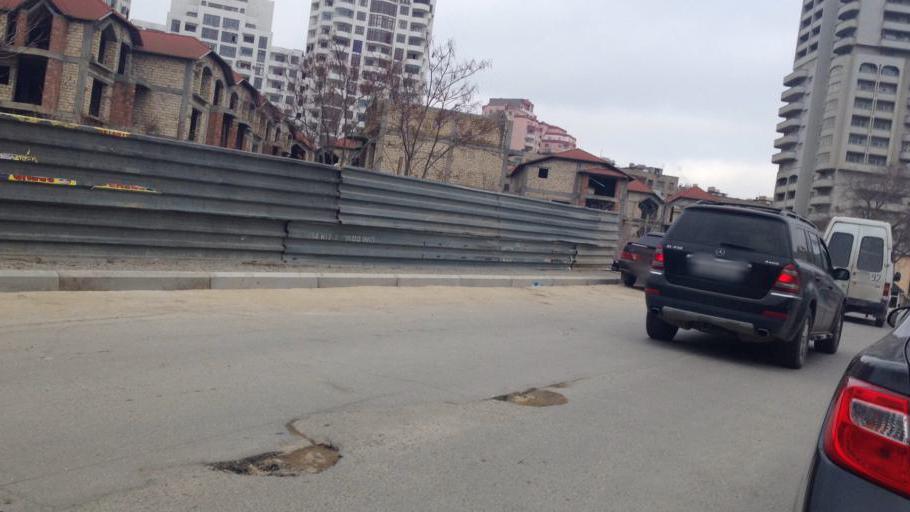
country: AZ
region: Baki
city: Bilajari
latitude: 40.3938
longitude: 49.8204
